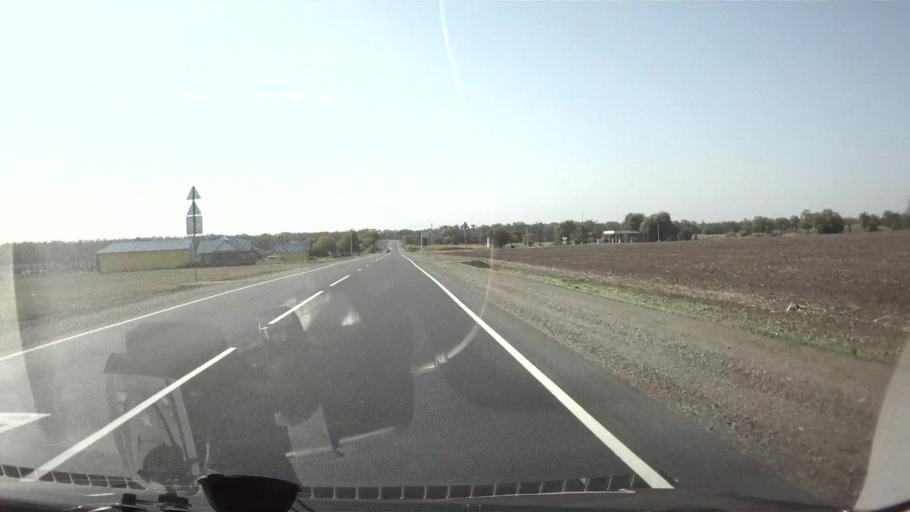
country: RU
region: Krasnodarskiy
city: Kavkazskaya
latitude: 45.5482
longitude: 40.6897
